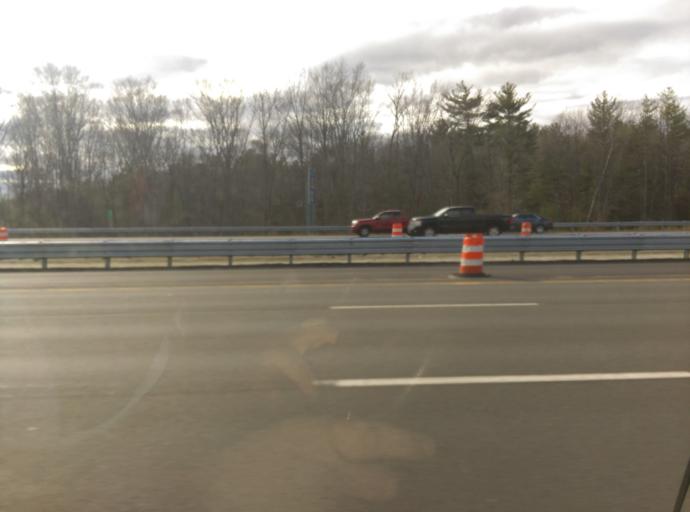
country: US
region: Massachusetts
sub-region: Essex County
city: Amesbury
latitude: 42.8486
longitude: -70.9006
